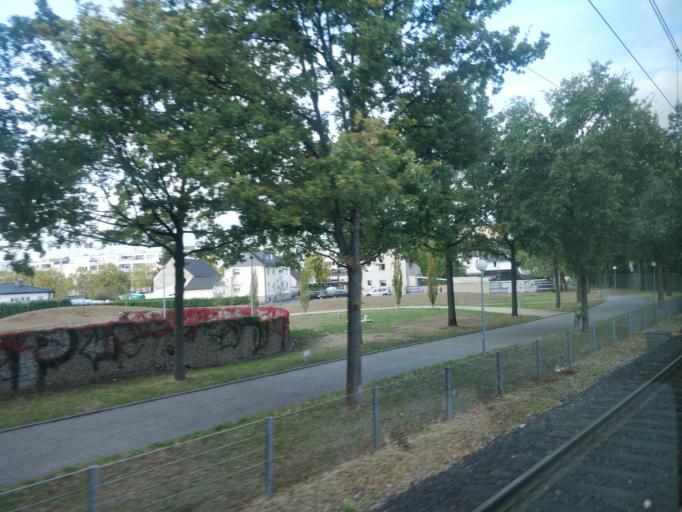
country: DE
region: North Rhine-Westphalia
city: Sankt Augustin
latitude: 50.7787
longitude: 7.1900
